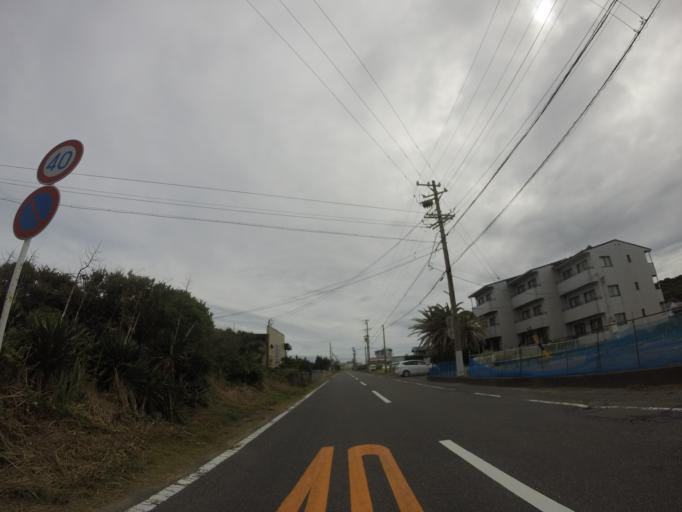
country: JP
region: Shizuoka
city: Oyama
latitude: 34.6023
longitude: 138.2333
